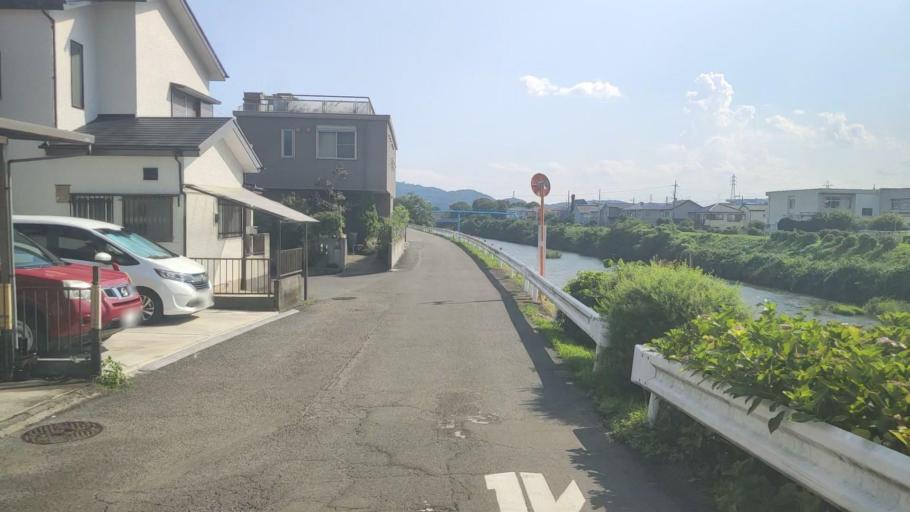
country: JP
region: Kanagawa
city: Hiratsuka
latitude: 35.3482
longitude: 139.3261
